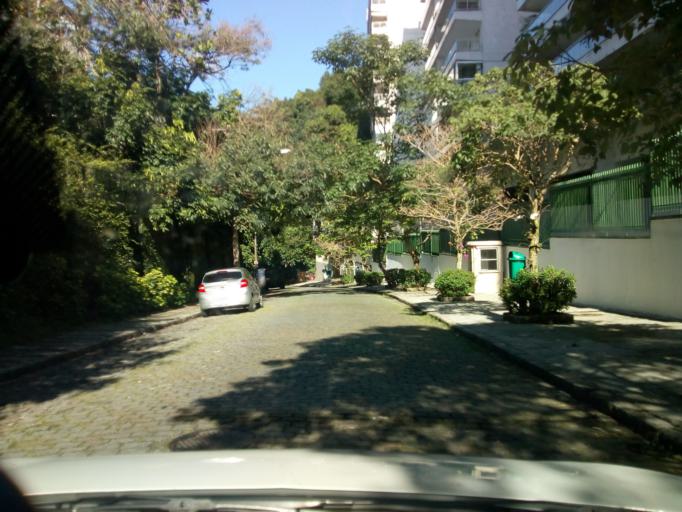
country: BR
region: Rio de Janeiro
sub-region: Rio De Janeiro
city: Rio de Janeiro
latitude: -22.9854
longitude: -43.2342
